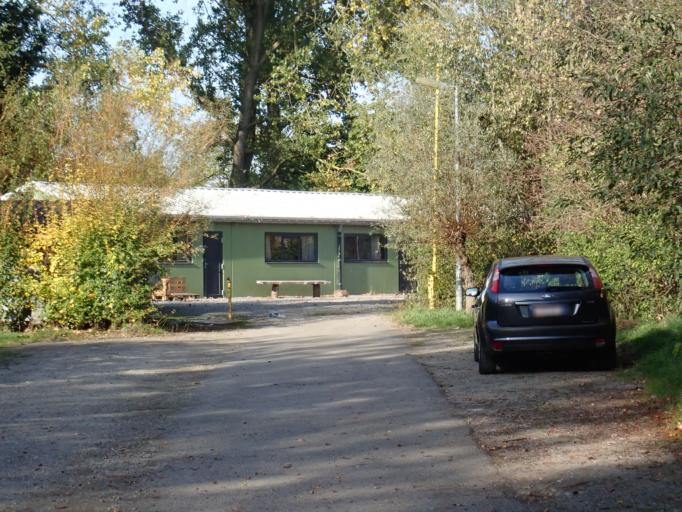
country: BE
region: Flanders
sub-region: Provincie Vlaams-Brabant
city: Holsbeek
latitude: 50.9425
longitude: 4.7460
